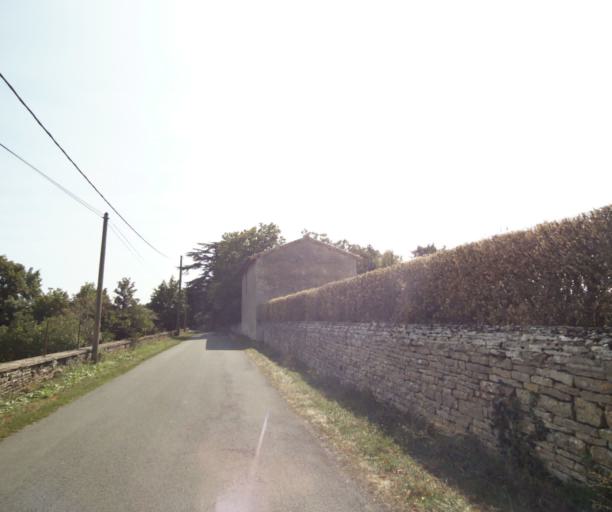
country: FR
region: Bourgogne
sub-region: Departement de Saone-et-Loire
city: Tournus
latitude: 46.5761
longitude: 4.8903
